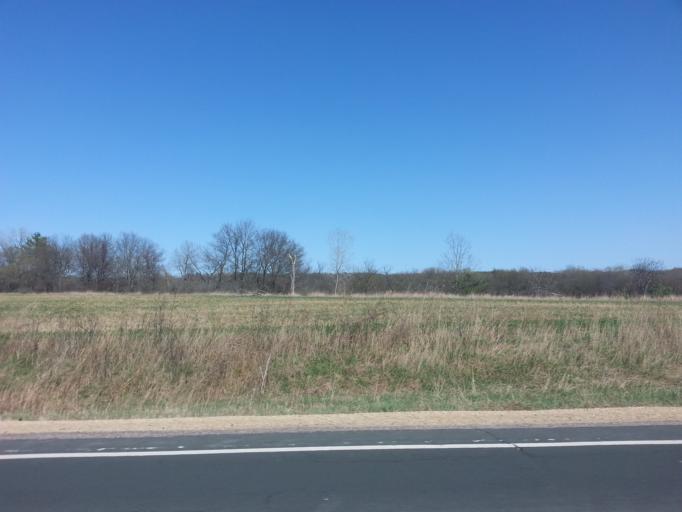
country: US
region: Wisconsin
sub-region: Dunn County
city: Menomonie
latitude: 44.7693
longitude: -91.9374
